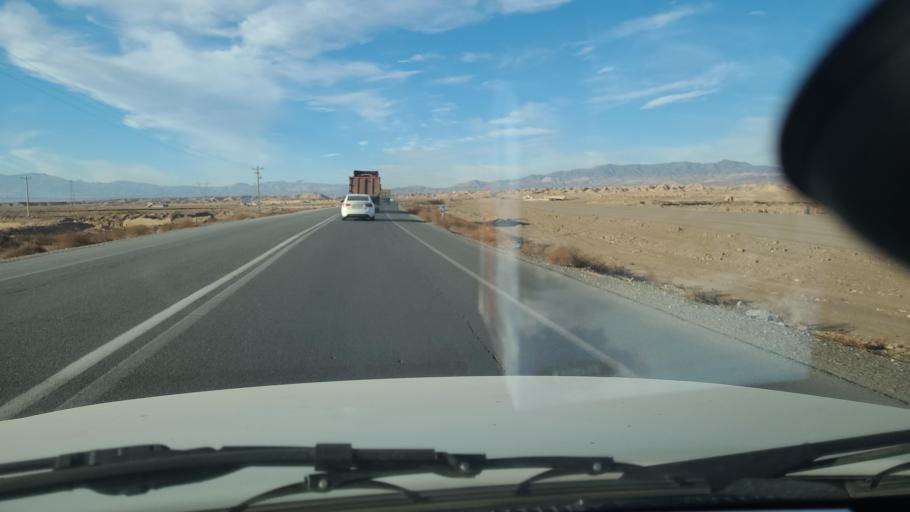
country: IR
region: Razavi Khorasan
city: Sabzevar
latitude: 36.2409
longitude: 57.6392
